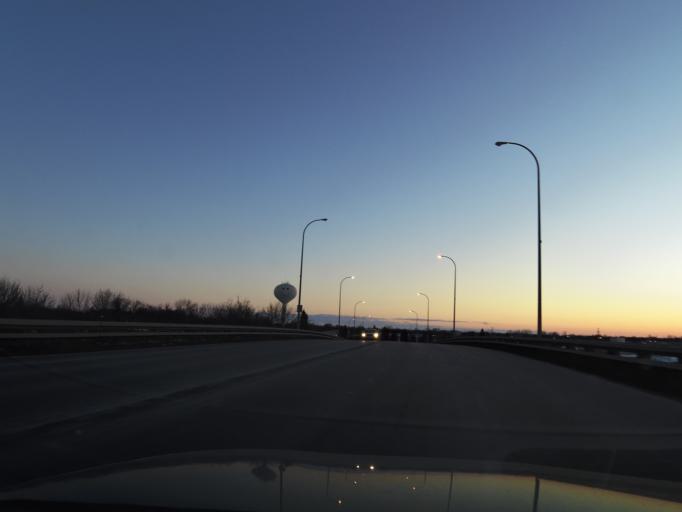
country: US
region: North Dakota
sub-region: Grand Forks County
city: Grand Forks
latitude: 47.9202
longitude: -97.0382
